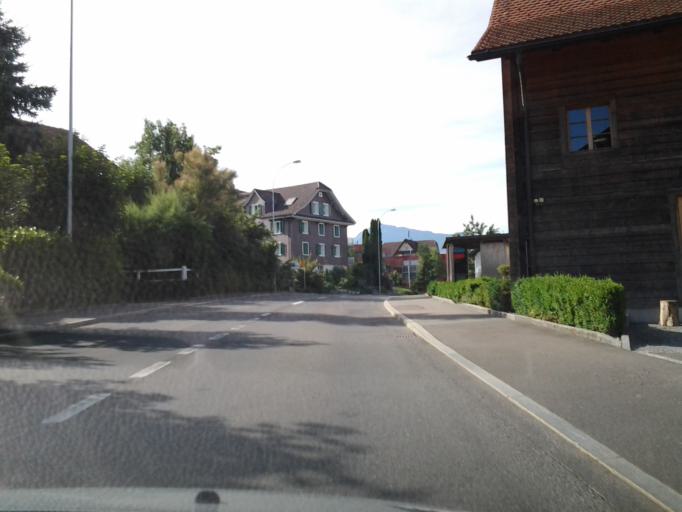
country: CH
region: Zug
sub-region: Zug
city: Hunenberg
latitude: 47.1547
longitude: 8.4400
